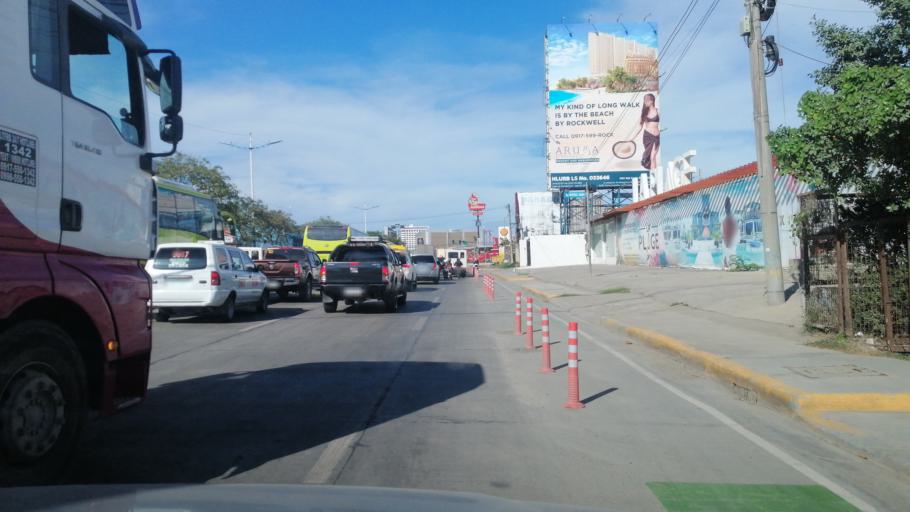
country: PH
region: Central Visayas
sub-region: Cebu City
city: Baugo
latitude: 10.3156
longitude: 123.9277
